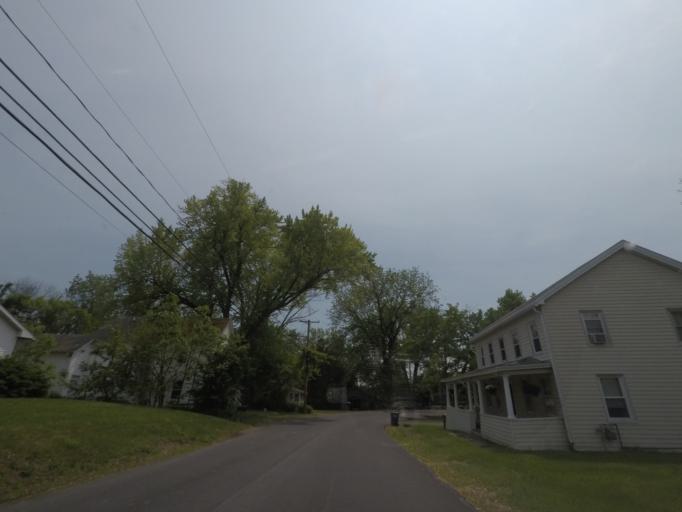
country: US
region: New York
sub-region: Rensselaer County
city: Castleton-on-Hudson
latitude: 42.5115
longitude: -73.7056
